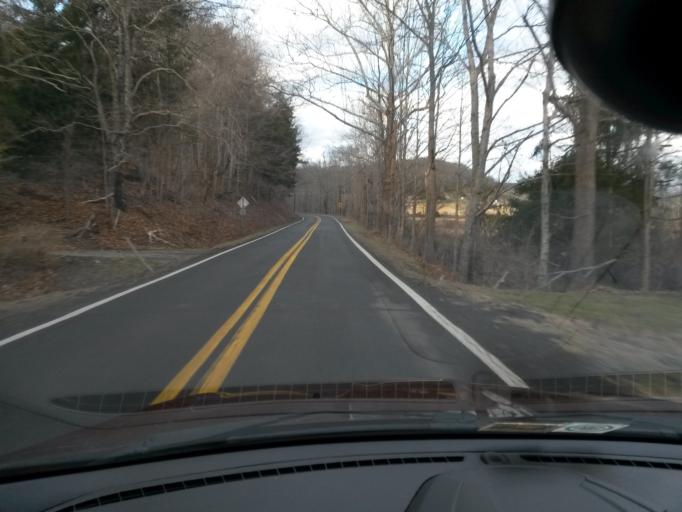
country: US
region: West Virginia
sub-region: Monroe County
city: Union
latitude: 37.5349
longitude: -80.5990
